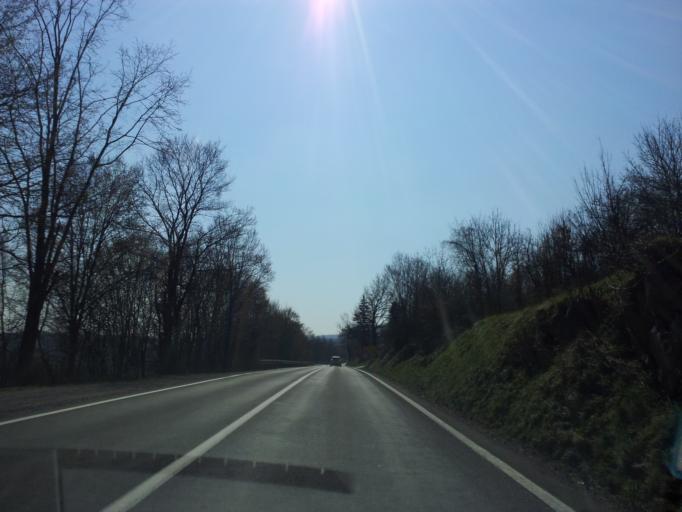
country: HR
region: Karlovacka
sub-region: Grad Karlovac
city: Slunj
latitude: 45.0976
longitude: 15.5919
